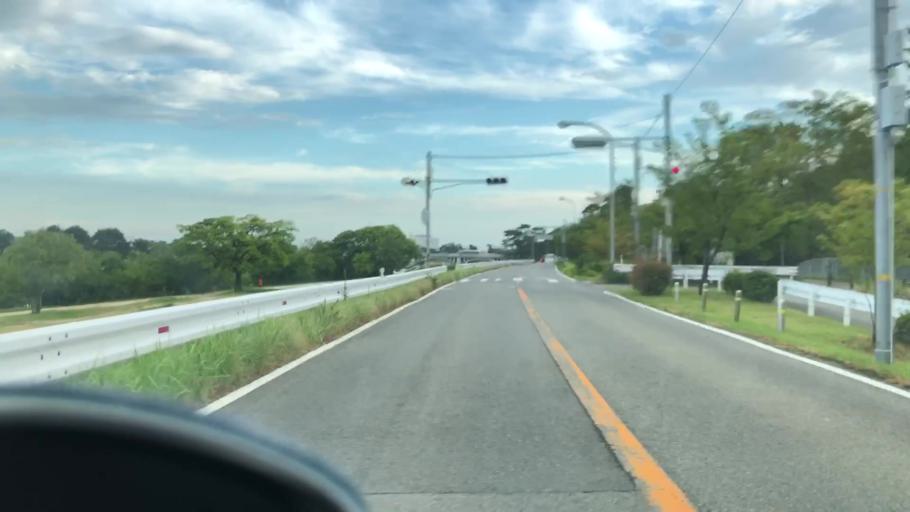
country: JP
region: Hyogo
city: Amagasaki
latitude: 34.7355
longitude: 135.3795
